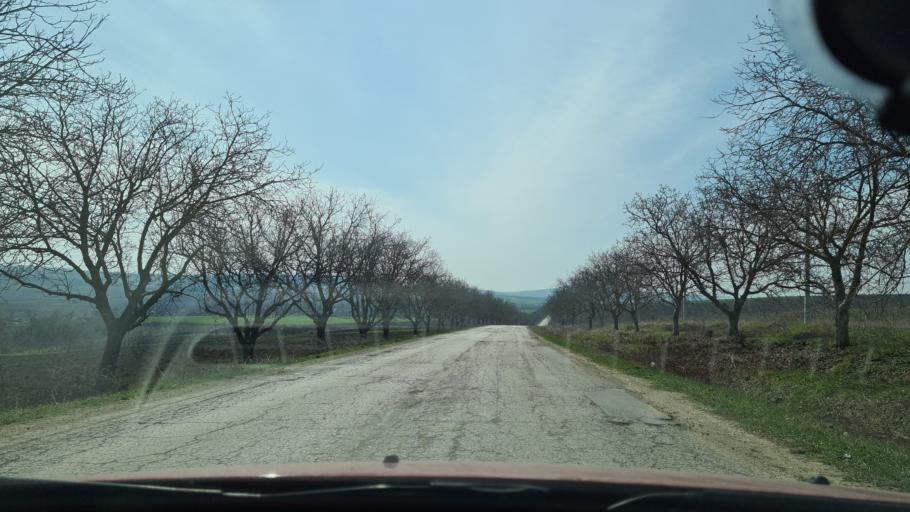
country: MD
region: Ungheni
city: Ungheni
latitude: 47.2864
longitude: 27.9229
